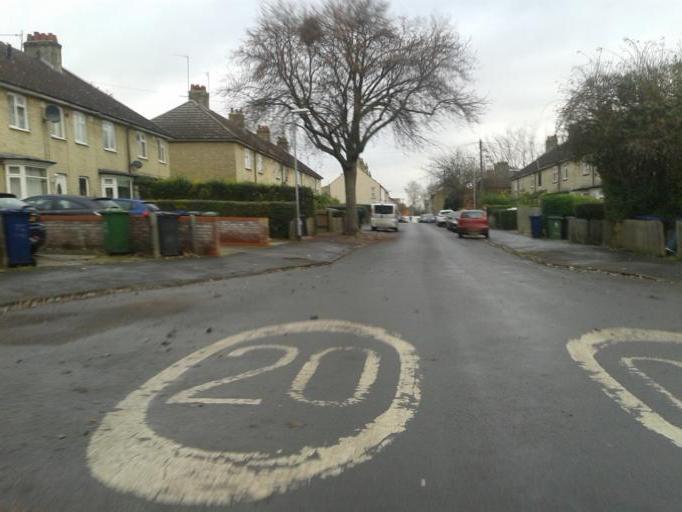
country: GB
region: England
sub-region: Cambridgeshire
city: Cambridge
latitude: 52.1944
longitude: 0.1516
